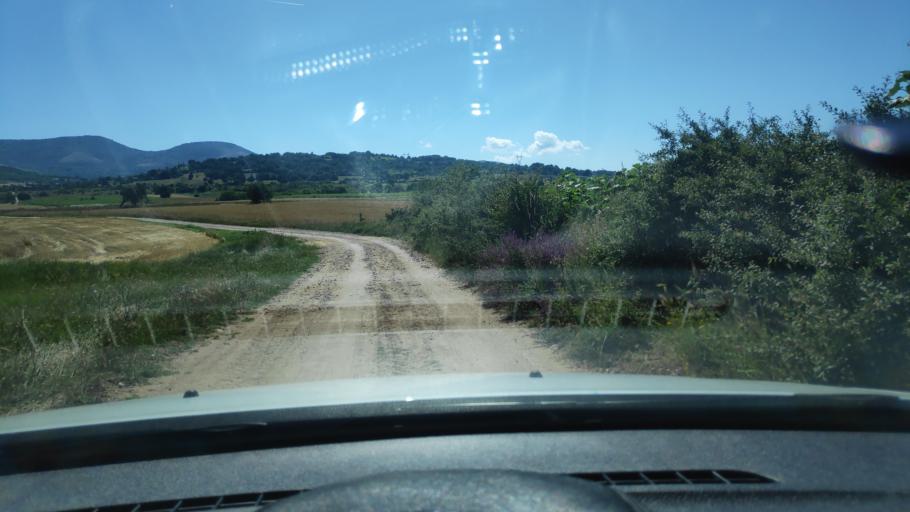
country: MK
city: Klechovce
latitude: 42.0673
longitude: 21.8616
